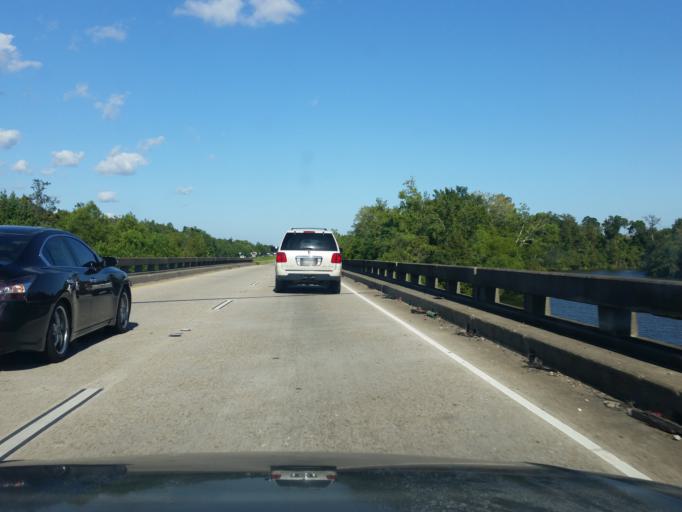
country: US
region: Mississippi
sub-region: Hancock County
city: Pearlington
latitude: 30.2982
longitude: -89.6637
